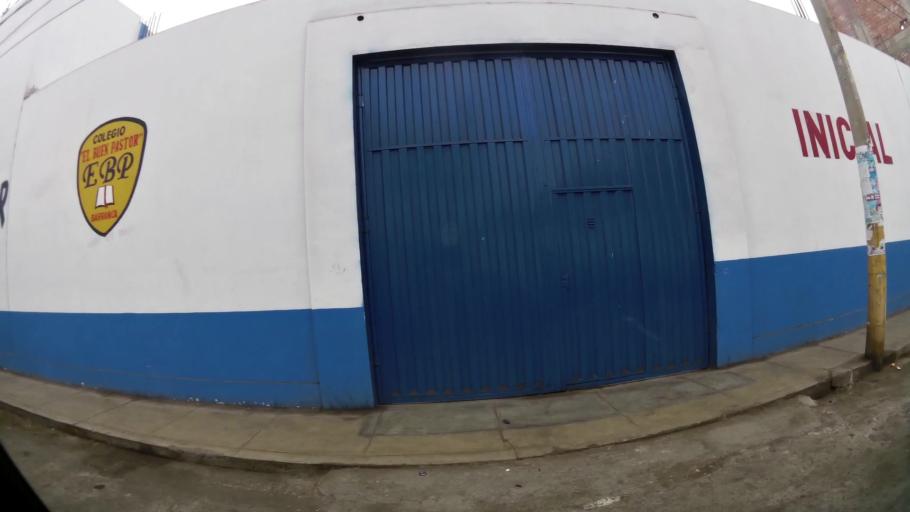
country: PE
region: Lima
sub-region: Barranca
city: Barranca
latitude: -10.7526
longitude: -77.7641
